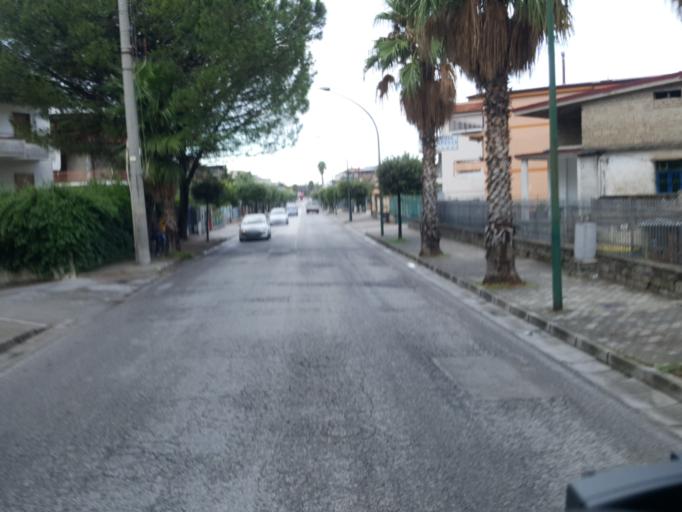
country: IT
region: Campania
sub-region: Provincia di Napoli
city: Palma Campania
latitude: 40.8568
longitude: 14.5531
